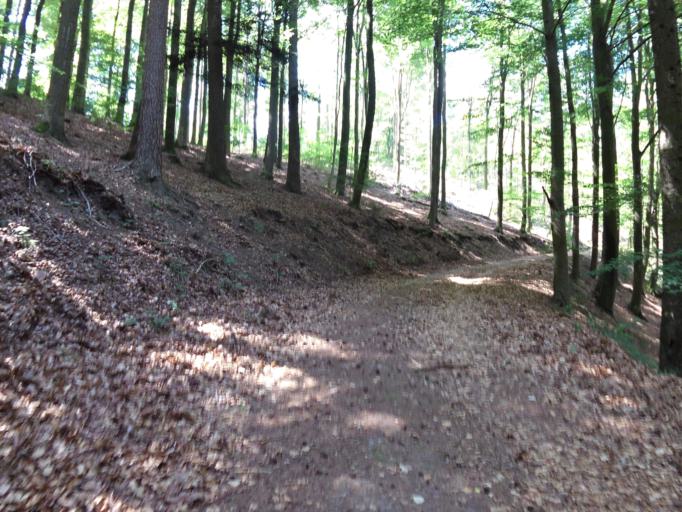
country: DE
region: Rheinland-Pfalz
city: Waldleiningen
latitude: 49.3748
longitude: 7.8587
